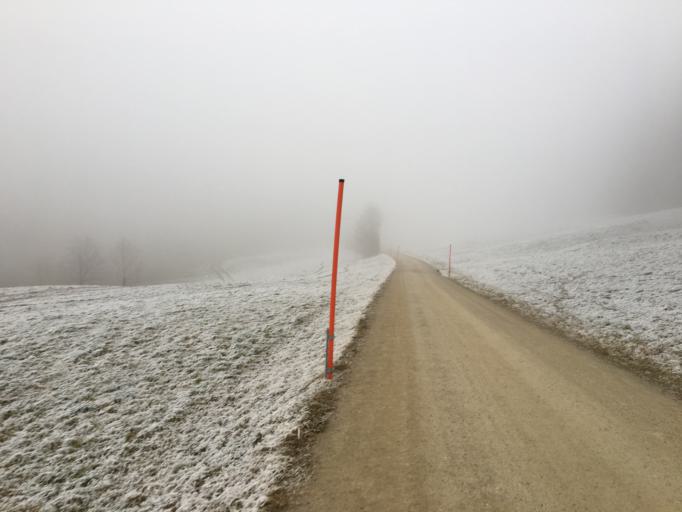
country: CH
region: Zurich
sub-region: Bezirk Horgen
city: Adliswil / Sonnenberg
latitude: 47.3069
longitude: 8.5051
